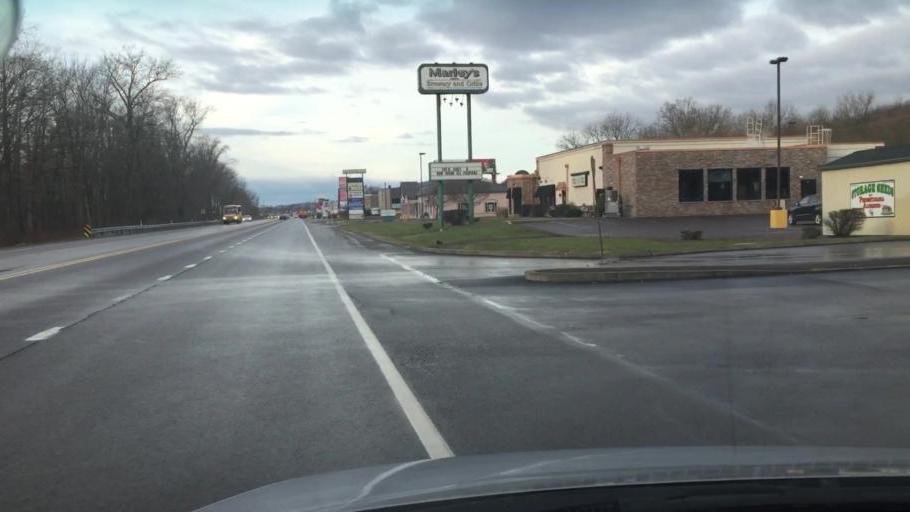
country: US
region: Pennsylvania
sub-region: Columbia County
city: Espy
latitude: 41.0067
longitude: -76.4301
